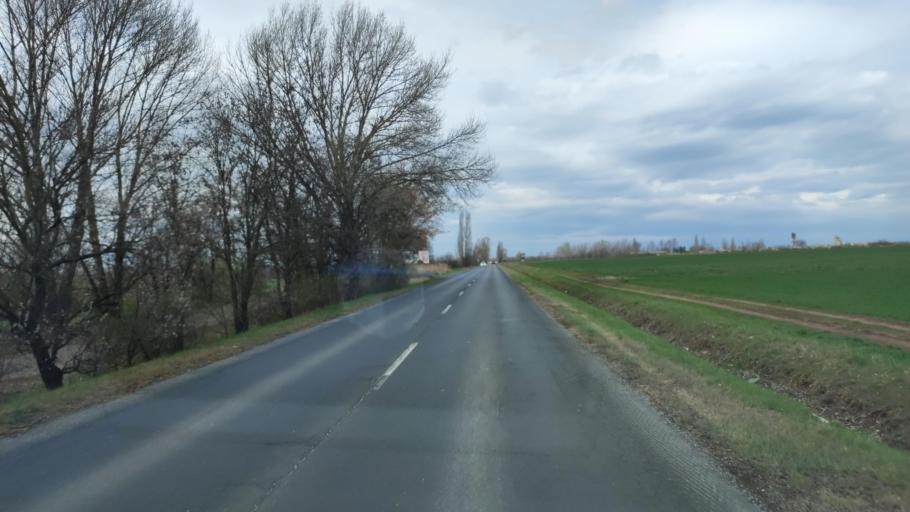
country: HU
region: Pest
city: Szazhalombatta
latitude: 47.3373
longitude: 18.9121
